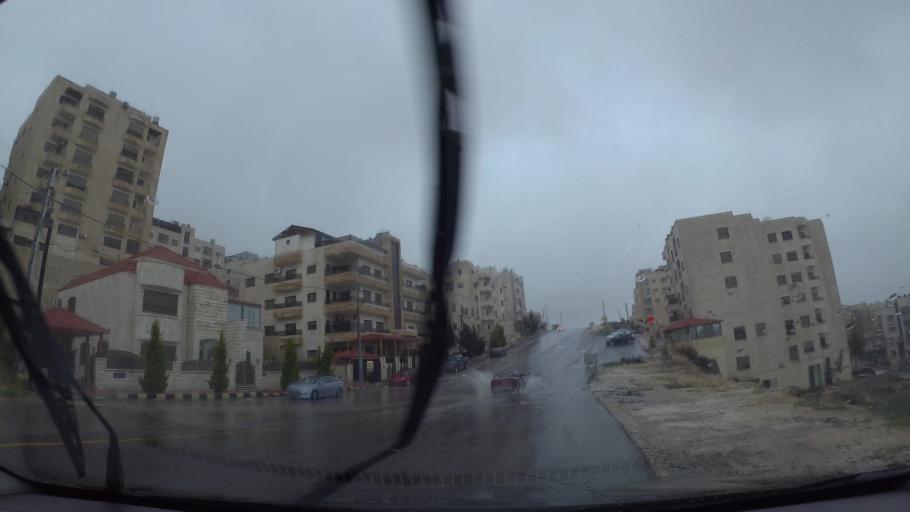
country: JO
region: Amman
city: Al Jubayhah
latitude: 32.0175
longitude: 35.8890
